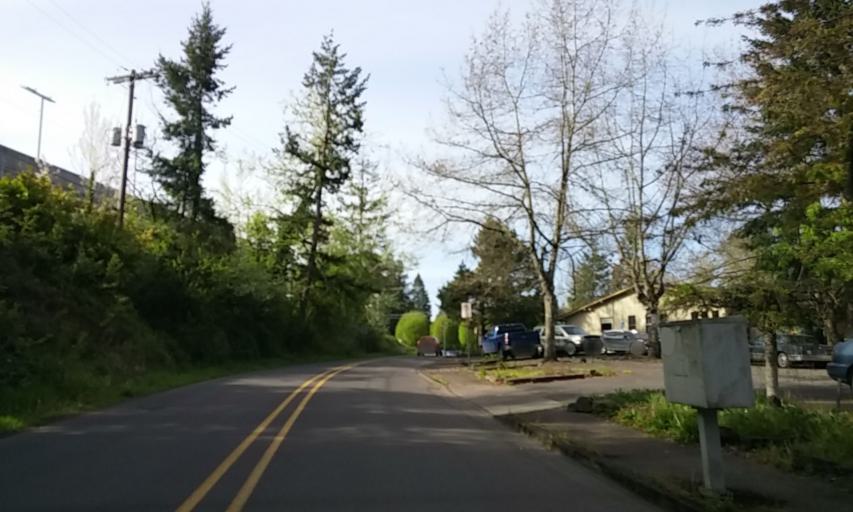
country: US
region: Oregon
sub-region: Washington County
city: West Slope
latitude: 45.4958
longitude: -122.7735
